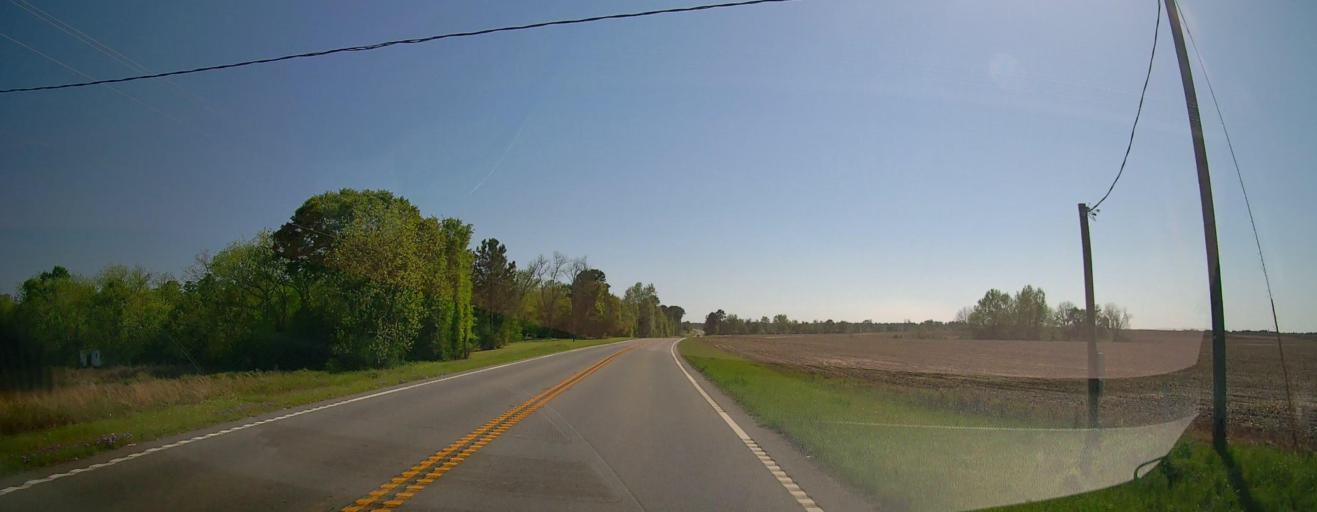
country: US
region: Georgia
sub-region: Pulaski County
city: Hawkinsville
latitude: 32.2144
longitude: -83.4835
